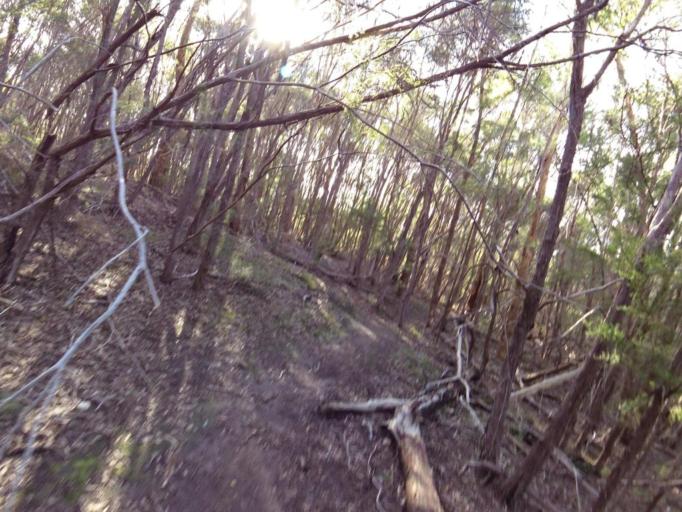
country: AU
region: Victoria
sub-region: Yarra Ranges
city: Chirnside Park
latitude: -37.7178
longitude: 145.2822
